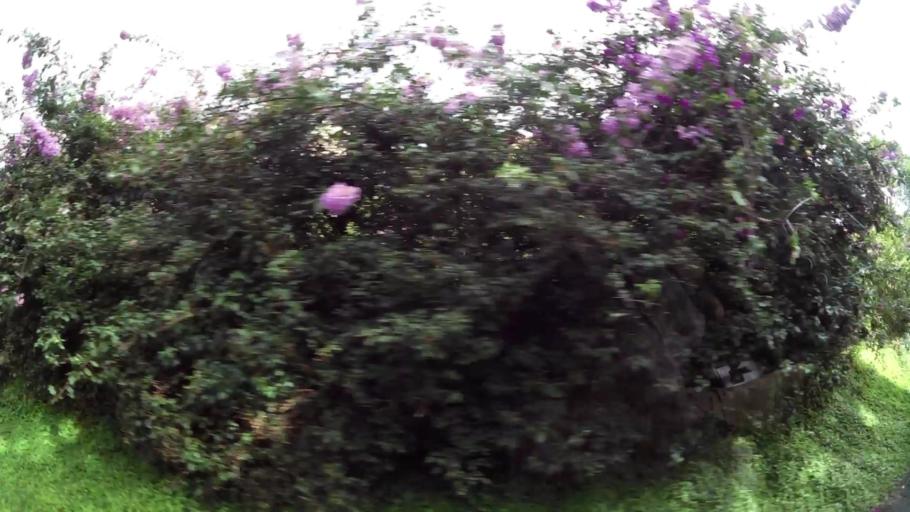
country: PA
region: Chiriqui
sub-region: Distrito Boquete
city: Boquete
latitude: 8.7960
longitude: -82.4342
